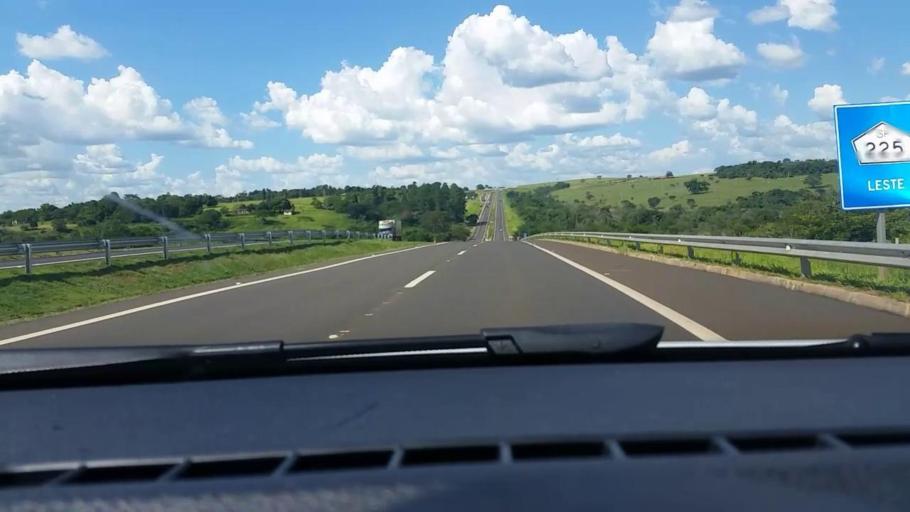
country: BR
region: Sao Paulo
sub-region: Bauru
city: Bauru
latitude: -22.4100
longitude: -49.1012
